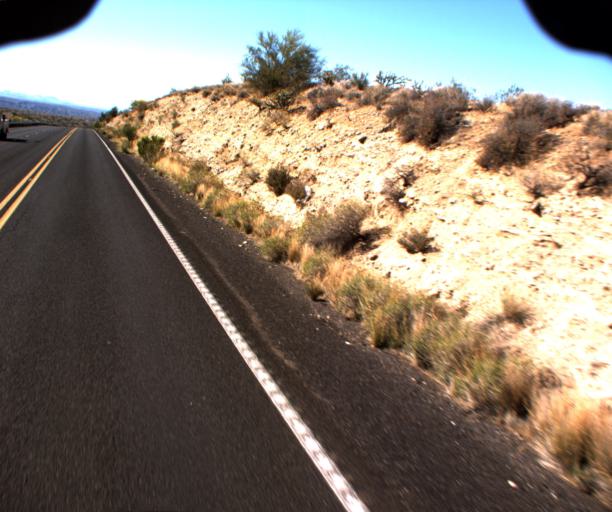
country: US
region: Arizona
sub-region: Mohave County
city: Kingman
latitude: 34.9354
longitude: -113.6620
